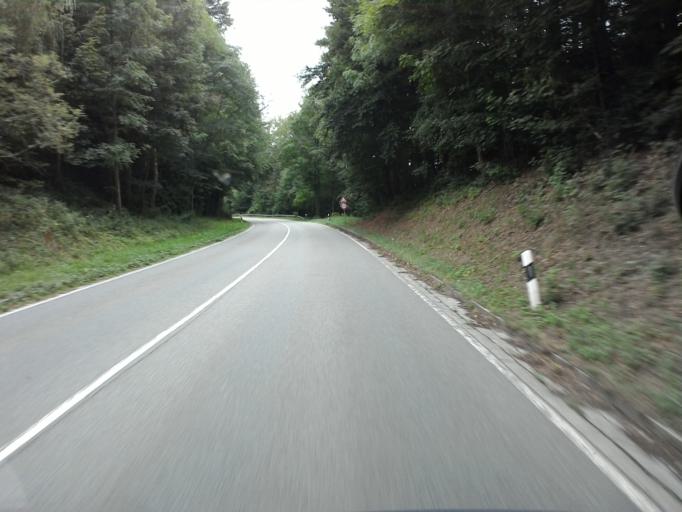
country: DE
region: Bavaria
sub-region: Upper Bavaria
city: Weyarn
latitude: 47.8464
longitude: 11.8097
